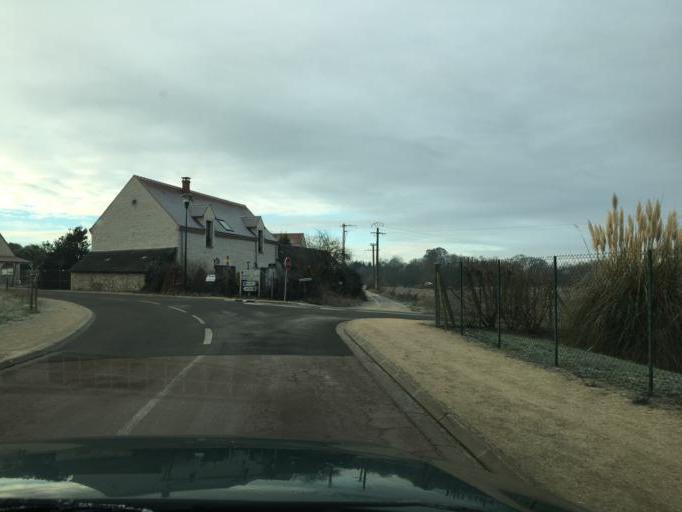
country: FR
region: Centre
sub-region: Departement du Loiret
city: Dry
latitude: 47.7923
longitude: 1.7079
